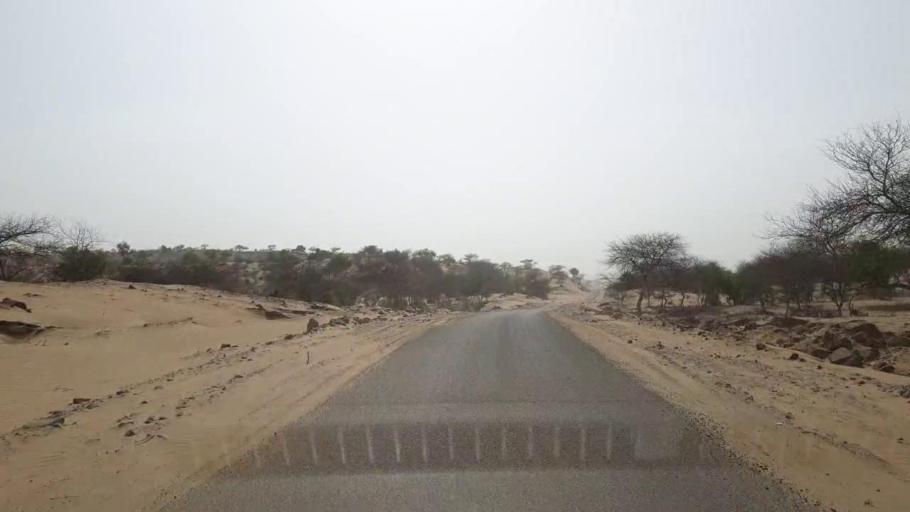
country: PK
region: Sindh
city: Mithi
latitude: 24.6188
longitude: 69.8833
